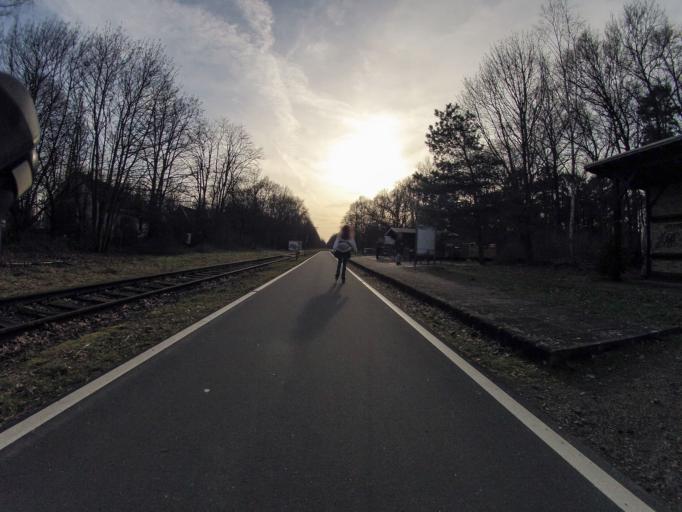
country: DE
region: North Rhine-Westphalia
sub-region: Regierungsbezirk Munster
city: Neuenkirchen
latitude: 52.2080
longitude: 7.4027
